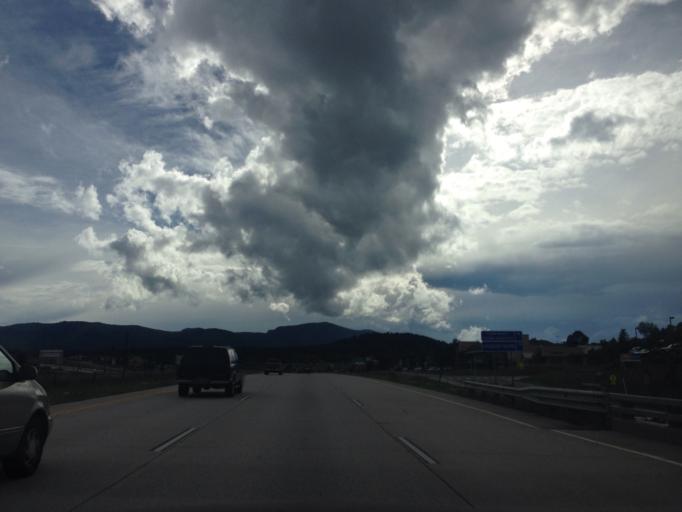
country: US
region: Colorado
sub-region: Jefferson County
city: Indian Hills
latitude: 39.5429
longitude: -105.2912
